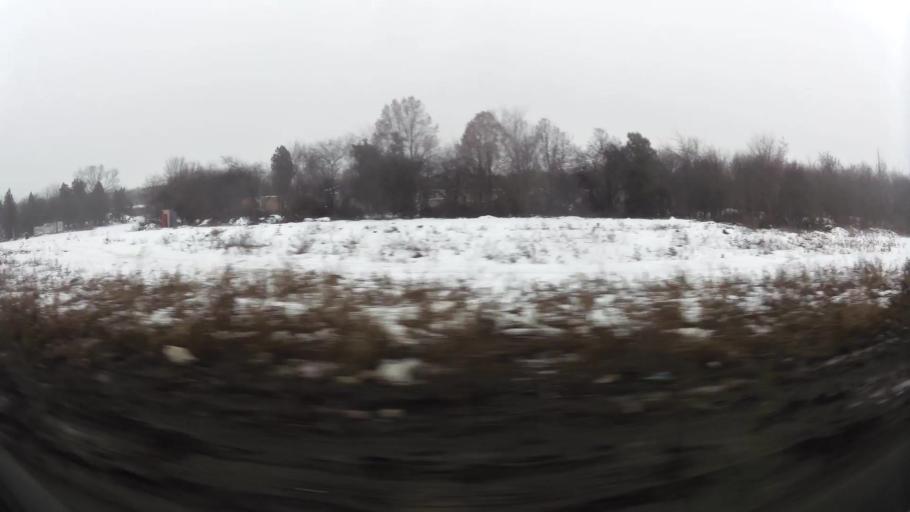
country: RO
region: Ilfov
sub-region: Comuna Clinceni
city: Olteni
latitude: 44.4041
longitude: 25.9774
